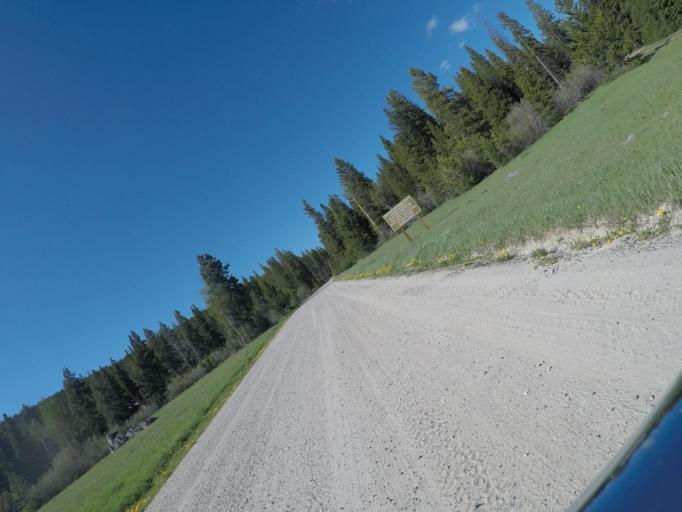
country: US
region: Wyoming
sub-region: Johnson County
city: Buffalo
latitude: 44.1896
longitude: -107.2481
